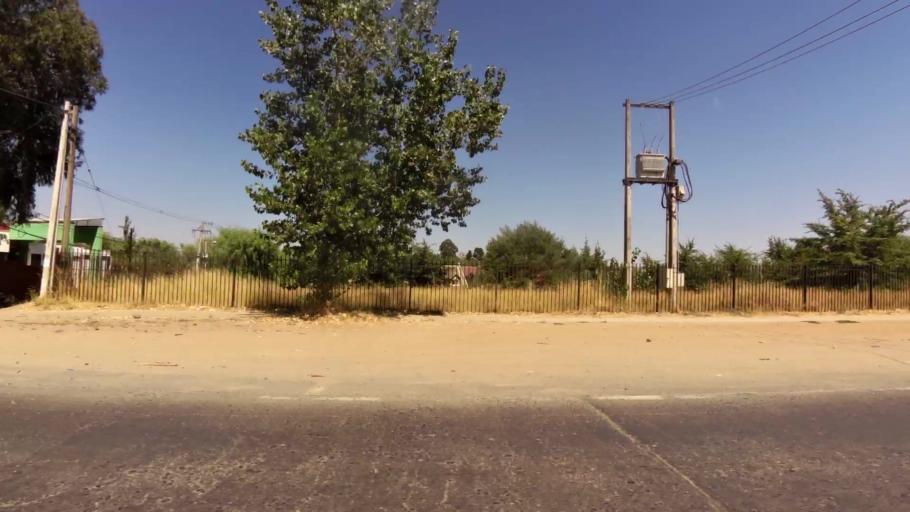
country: CL
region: Maule
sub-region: Provincia de Talca
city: Talca
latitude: -35.4059
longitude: -71.6437
